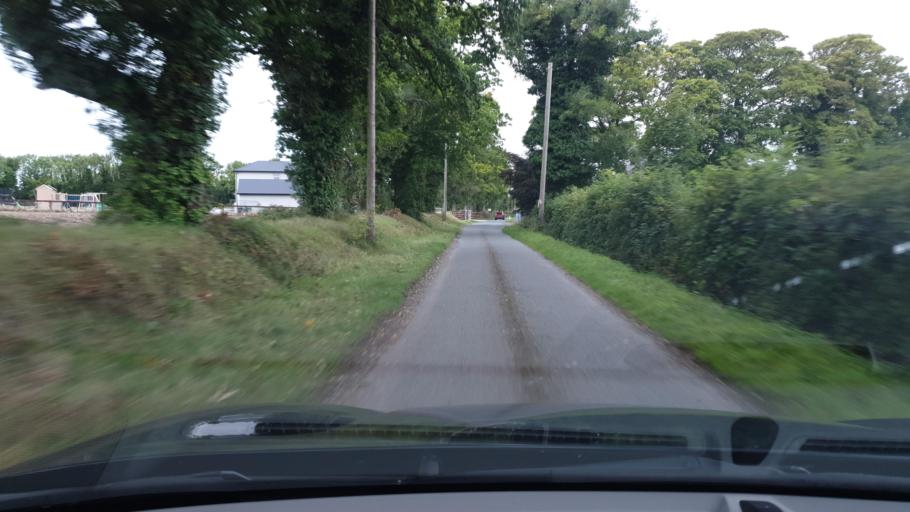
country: IE
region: Leinster
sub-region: An Mhi
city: Ratoath
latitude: 53.5250
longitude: -6.4969
